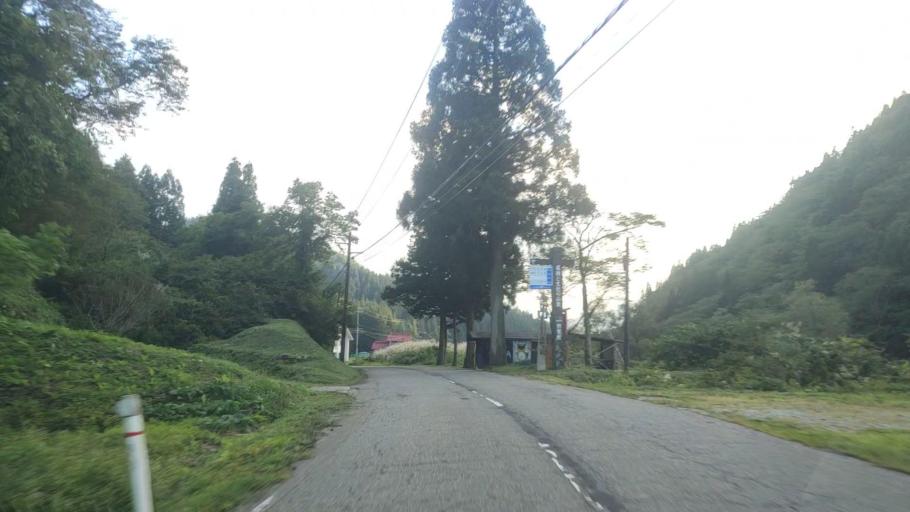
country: JP
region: Toyama
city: Yatsuomachi-higashikumisaka
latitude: 36.4705
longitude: 137.0486
